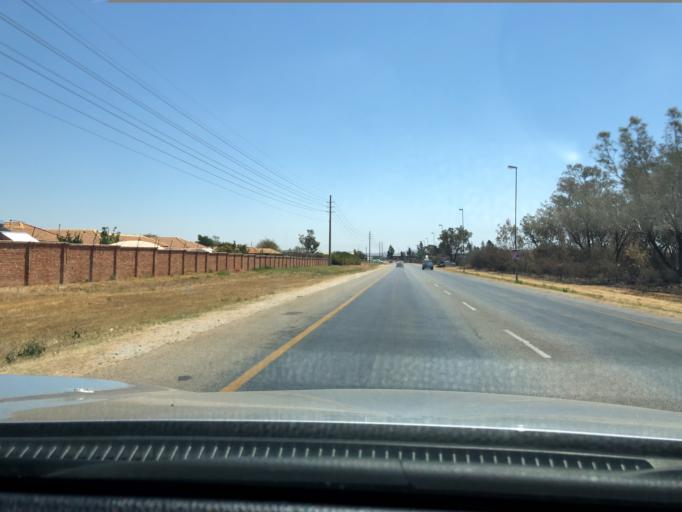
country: ZA
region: Limpopo
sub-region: Capricorn District Municipality
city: Polokwane
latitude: -23.8730
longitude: 29.4872
